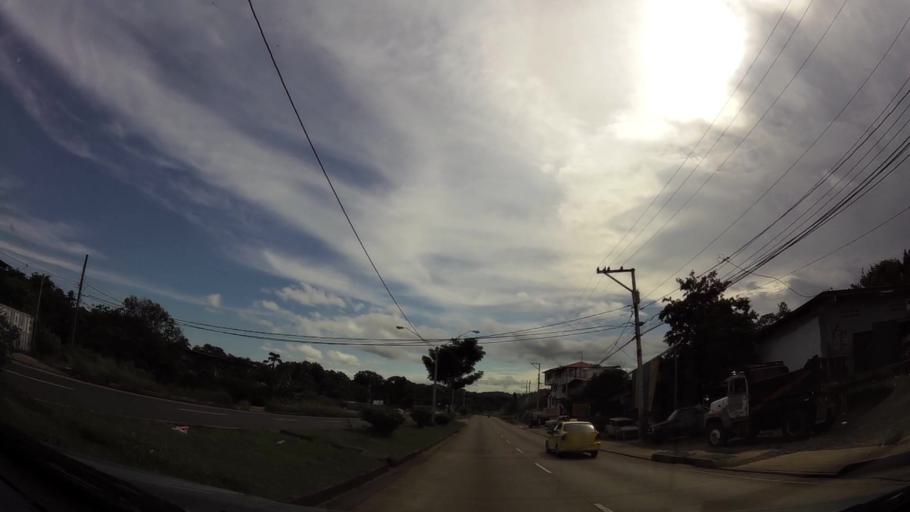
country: PA
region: Panama
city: El Coco
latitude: 8.8685
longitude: -79.8022
